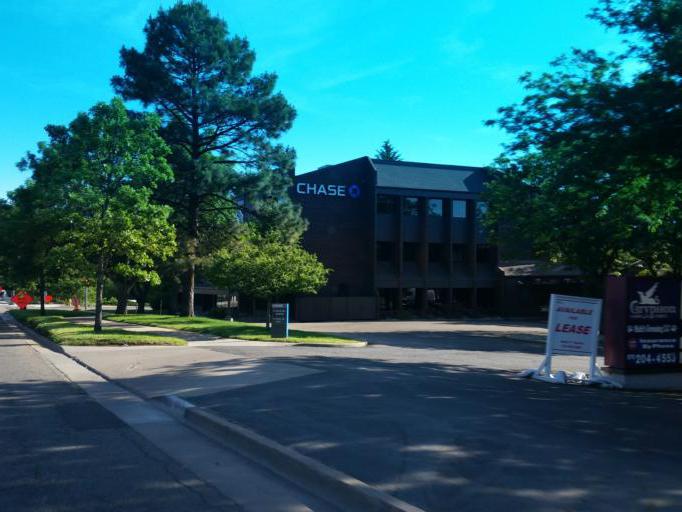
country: US
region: Colorado
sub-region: Larimer County
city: Fort Collins
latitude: 40.5610
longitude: -105.0769
